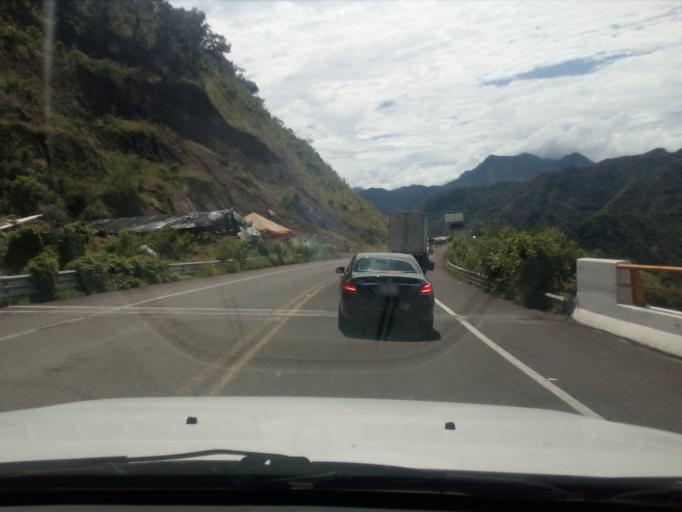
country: MX
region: Durango
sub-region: Pueblo Nuevo
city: La Ciudad
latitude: 23.5455
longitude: -105.7557
